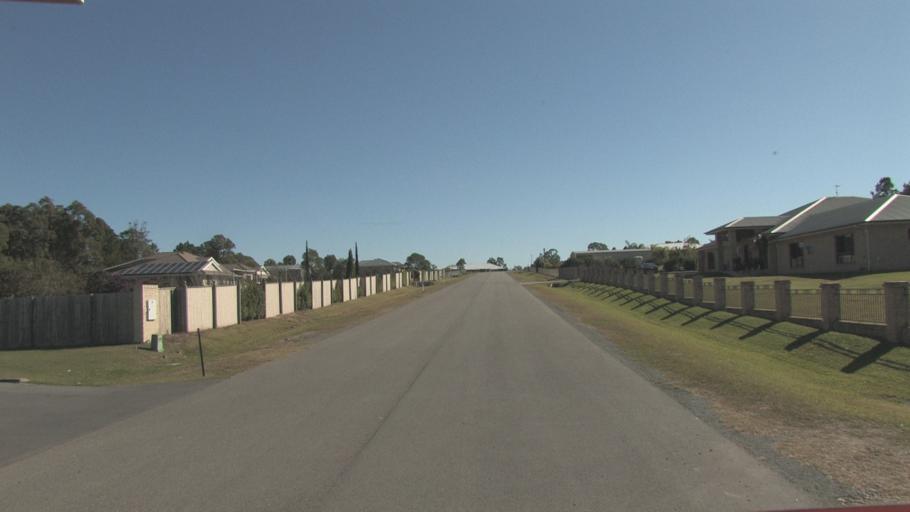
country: AU
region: Queensland
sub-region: Logan
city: Logan Reserve
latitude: -27.7274
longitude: 153.1248
